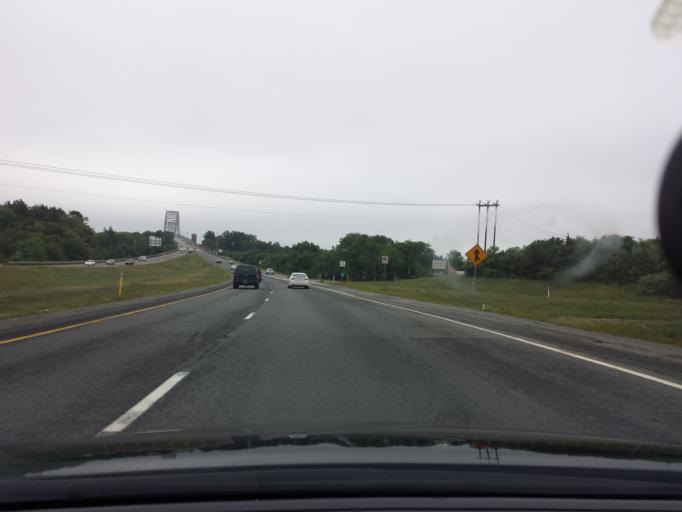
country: US
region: Massachusetts
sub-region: Barnstable County
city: Bourne
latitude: 41.7553
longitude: -70.5943
